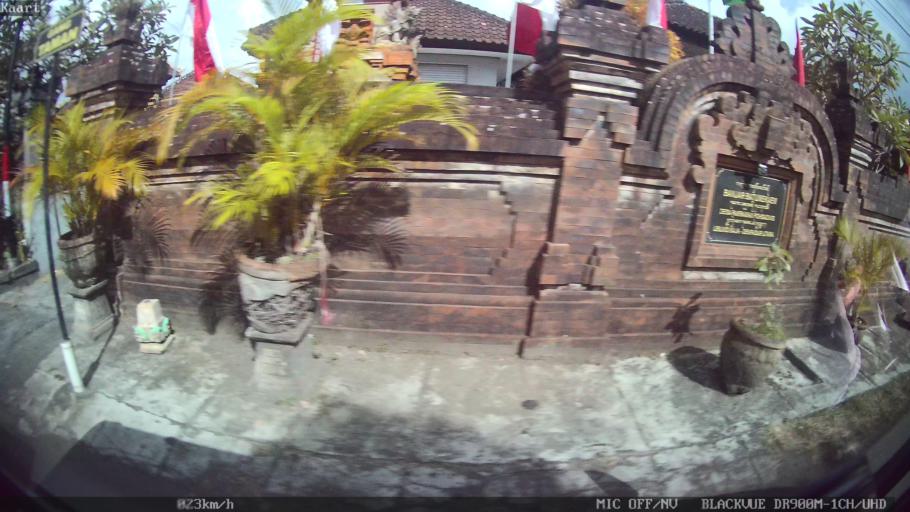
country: ID
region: Bali
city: Banjar Karangsuling
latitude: -8.6123
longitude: 115.2001
